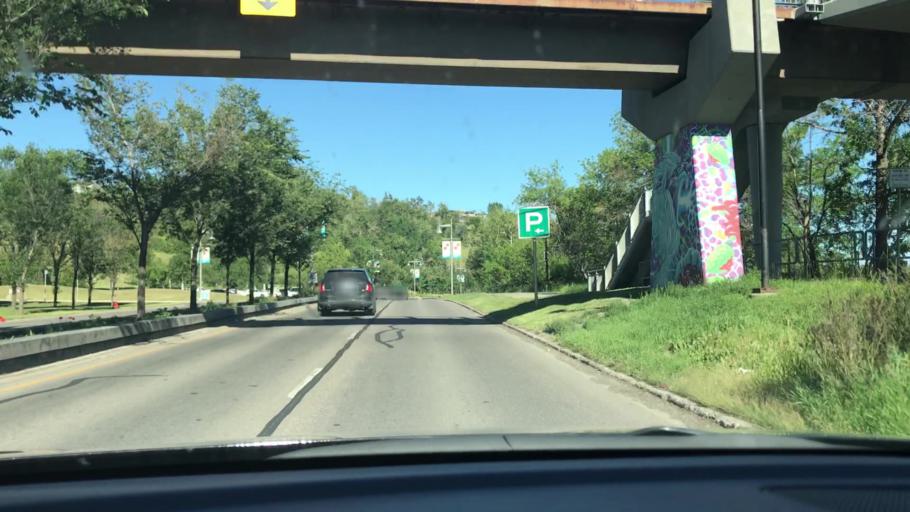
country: CA
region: Alberta
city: Calgary
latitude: 51.0575
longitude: -114.0695
